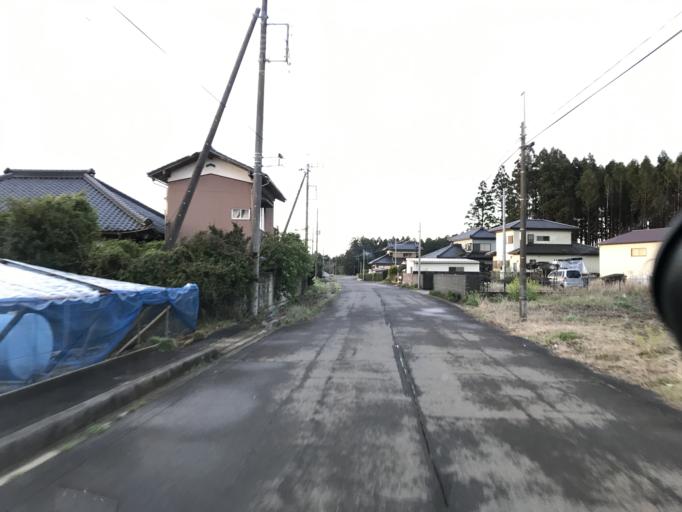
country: JP
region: Chiba
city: Sawara
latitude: 35.8283
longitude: 140.4954
